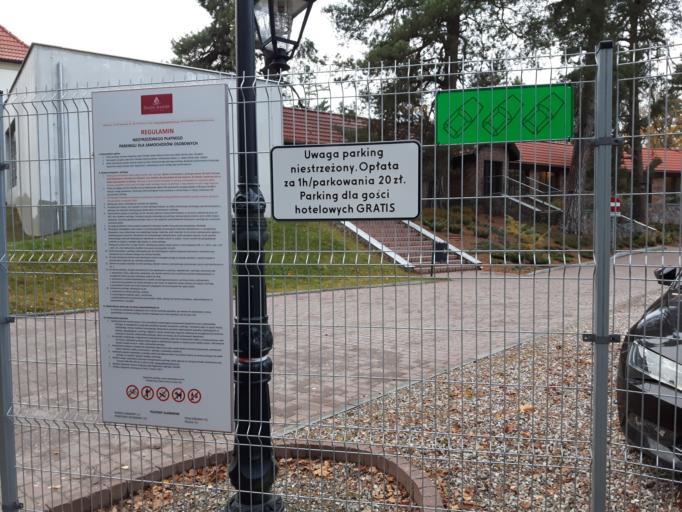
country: PL
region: Warmian-Masurian Voivodeship
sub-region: Powiat olsztynski
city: Barczewo
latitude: 53.8306
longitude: 20.7387
